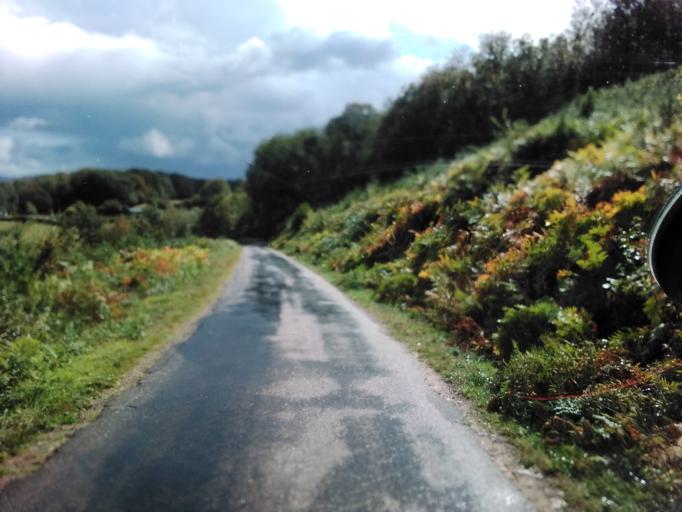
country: FR
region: Bourgogne
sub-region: Departement de la Nievre
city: Lormes
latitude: 47.3035
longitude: 3.8918
